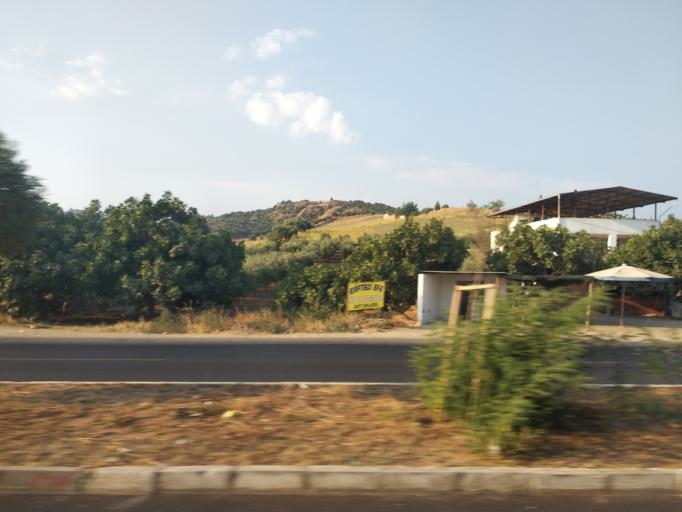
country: TR
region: Manisa
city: Ahmetli
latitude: 38.5090
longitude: 27.9821
